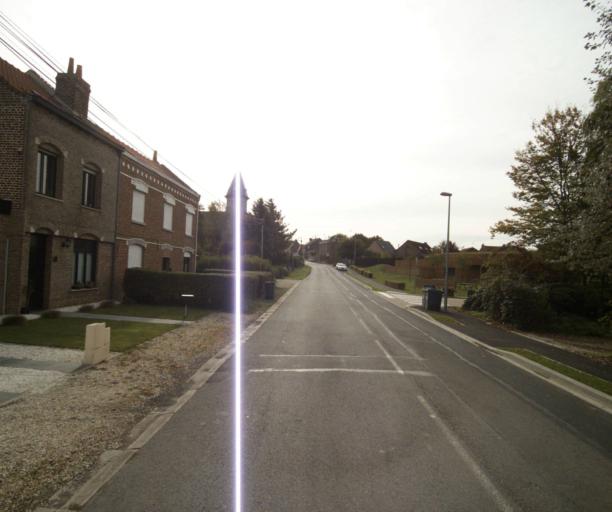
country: FR
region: Nord-Pas-de-Calais
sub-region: Departement du Nord
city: Aubers
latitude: 50.6088
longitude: 2.8517
